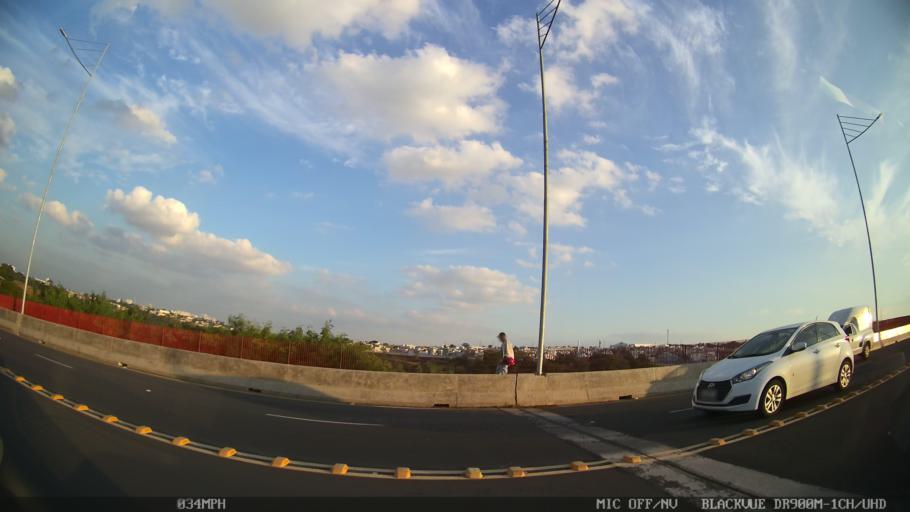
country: BR
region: Sao Paulo
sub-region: Hortolandia
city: Hortolandia
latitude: -22.8779
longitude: -47.1876
